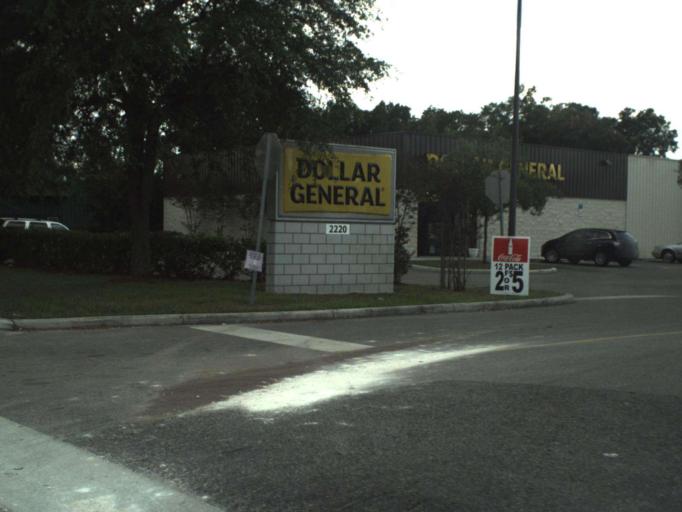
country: US
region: Florida
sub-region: Seminole County
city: Sanford
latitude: 28.7916
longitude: -81.2732
